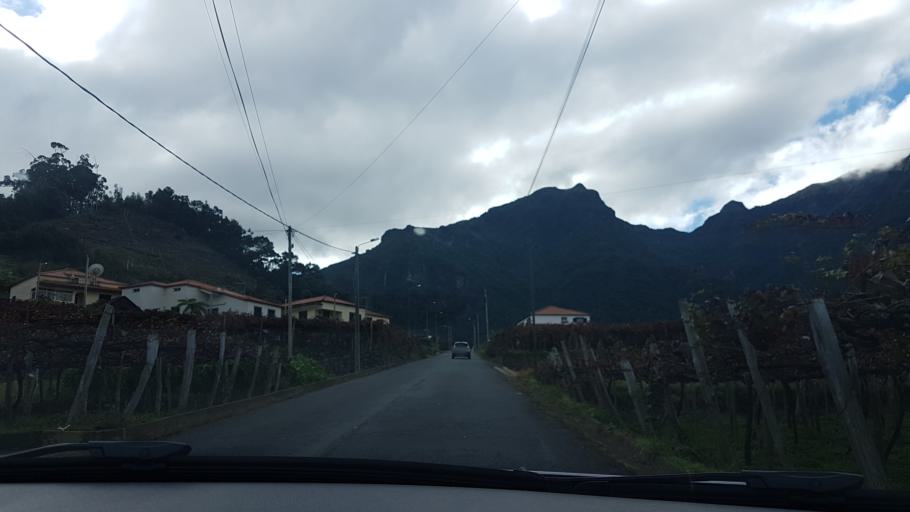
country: PT
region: Madeira
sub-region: Sao Vicente
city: Sao Vicente
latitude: 32.7796
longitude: -17.0293
